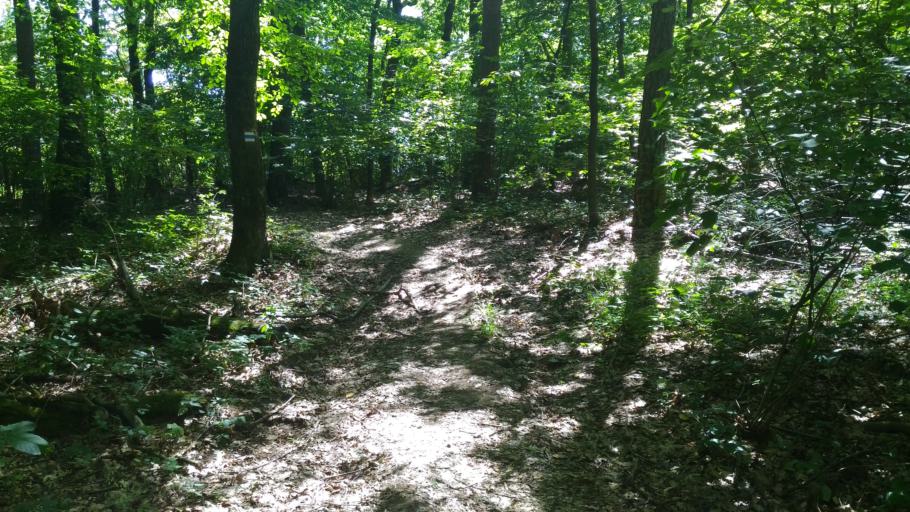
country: SI
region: Kobilje
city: Kobilje
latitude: 46.7265
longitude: 16.3820
